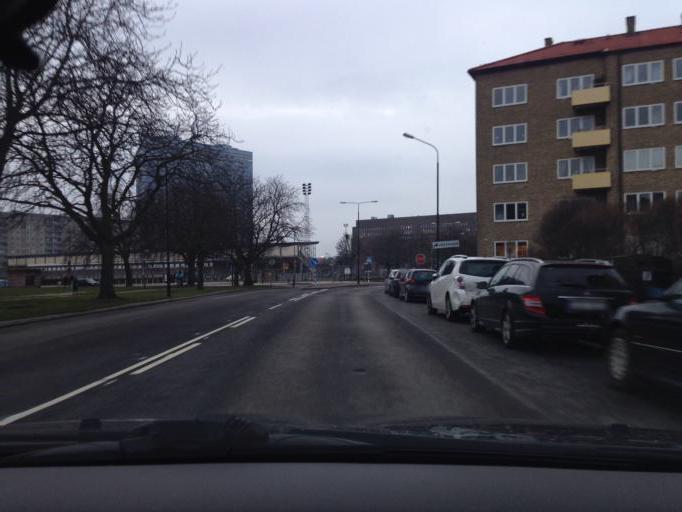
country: SE
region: Skane
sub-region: Malmo
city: Malmoe
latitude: 55.5966
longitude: 12.9904
